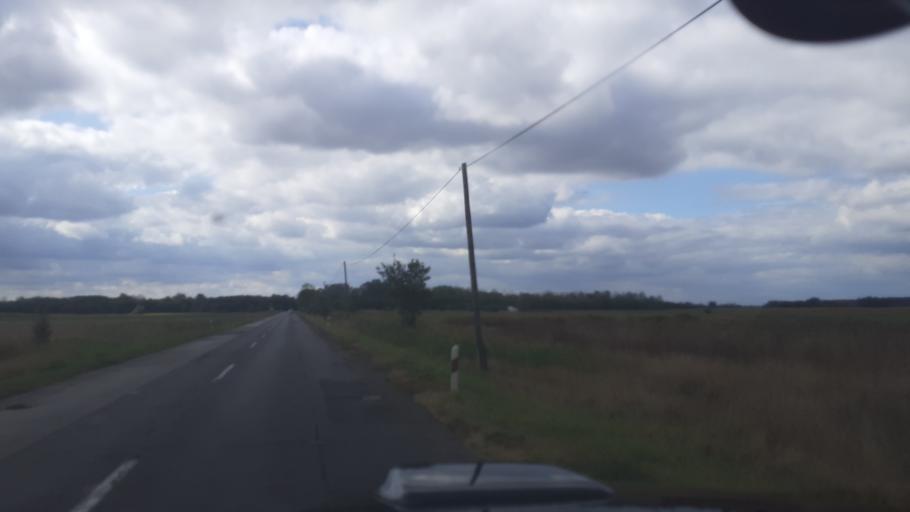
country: HU
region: Bacs-Kiskun
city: Fulopszallas
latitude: 46.8034
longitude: 19.1505
